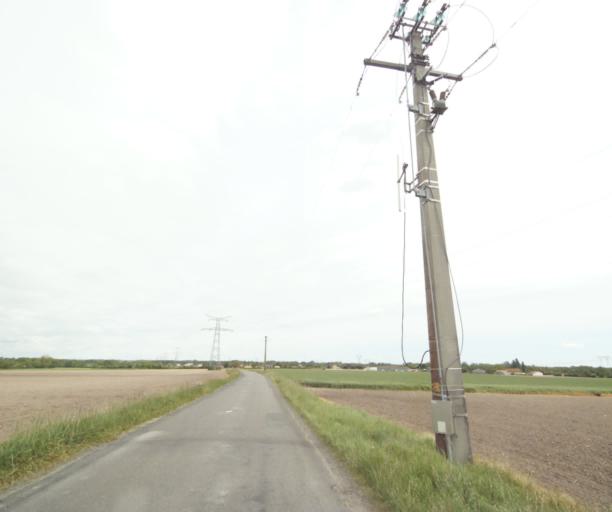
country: FR
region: Poitou-Charentes
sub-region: Departement de la Charente-Maritime
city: Les Gonds
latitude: 45.6902
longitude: -0.6044
